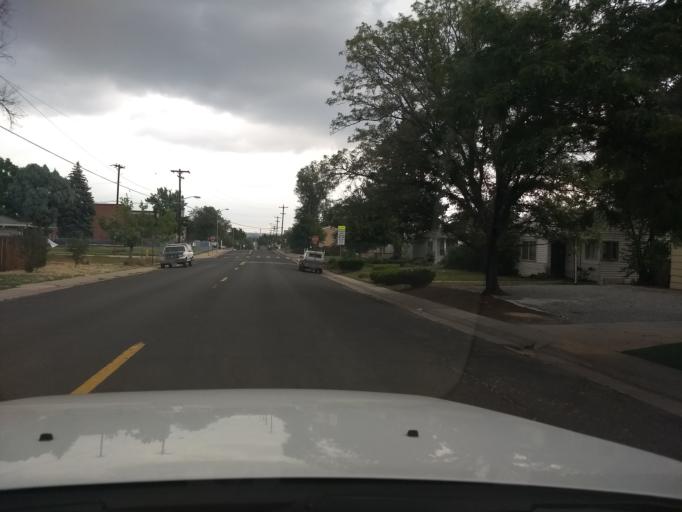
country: US
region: Colorado
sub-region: Denver County
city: Denver
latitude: 39.7068
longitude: -105.0110
